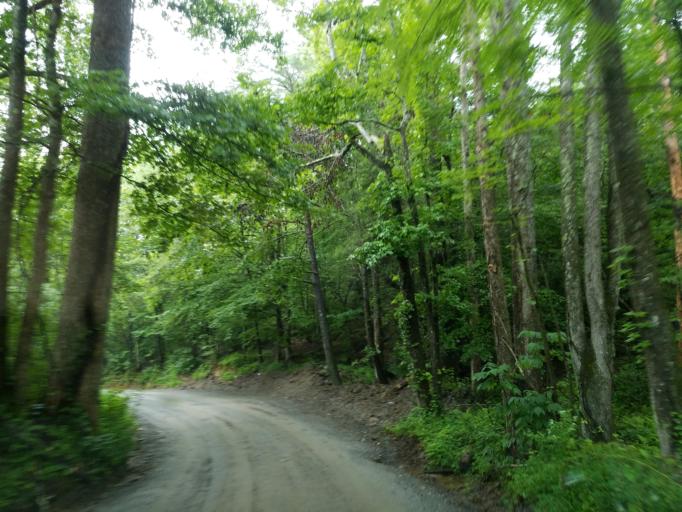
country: US
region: Georgia
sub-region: Fannin County
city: Blue Ridge
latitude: 34.7846
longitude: -84.3439
